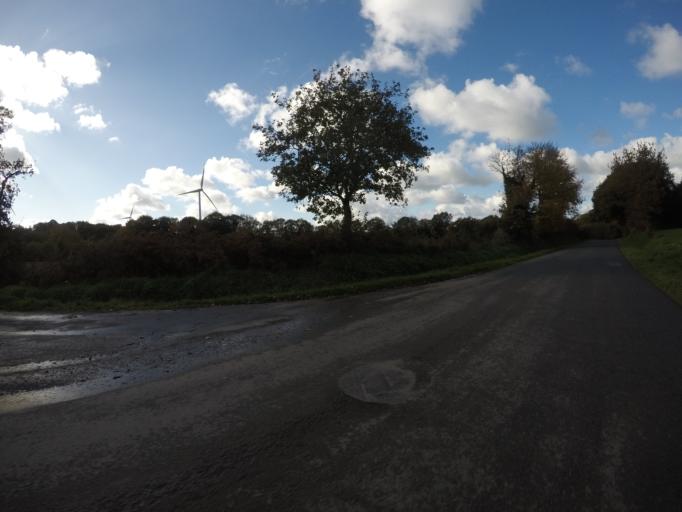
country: FR
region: Brittany
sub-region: Departement des Cotes-d'Armor
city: Bourbriac
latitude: 48.4623
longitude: -3.2466
